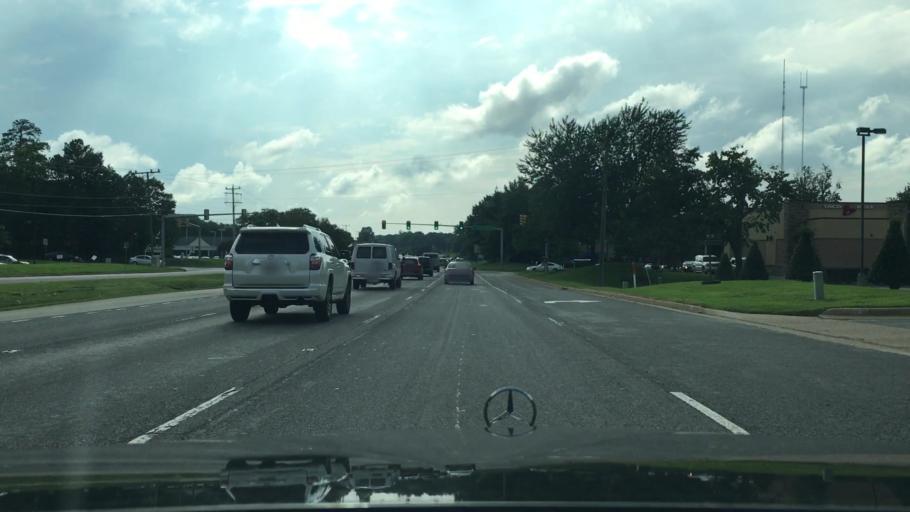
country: US
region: Virginia
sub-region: Chesterfield County
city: Bon Air
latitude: 37.5068
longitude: -77.5852
